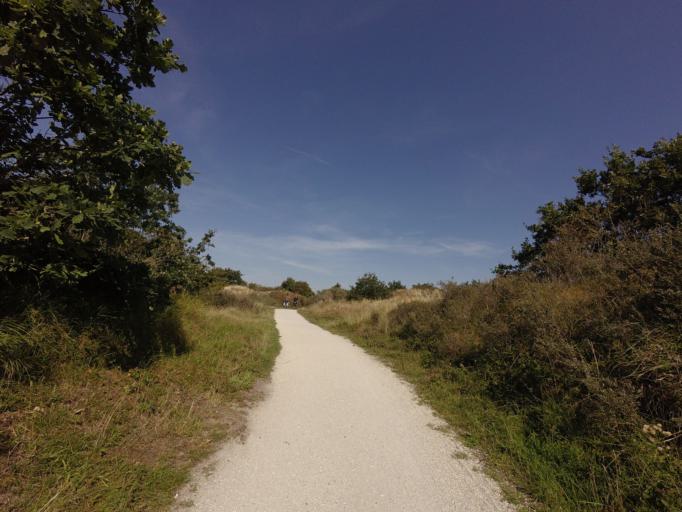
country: NL
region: Friesland
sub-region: Gemeente Schiermonnikoog
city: Schiermonnikoog
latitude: 53.4788
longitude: 6.1444
